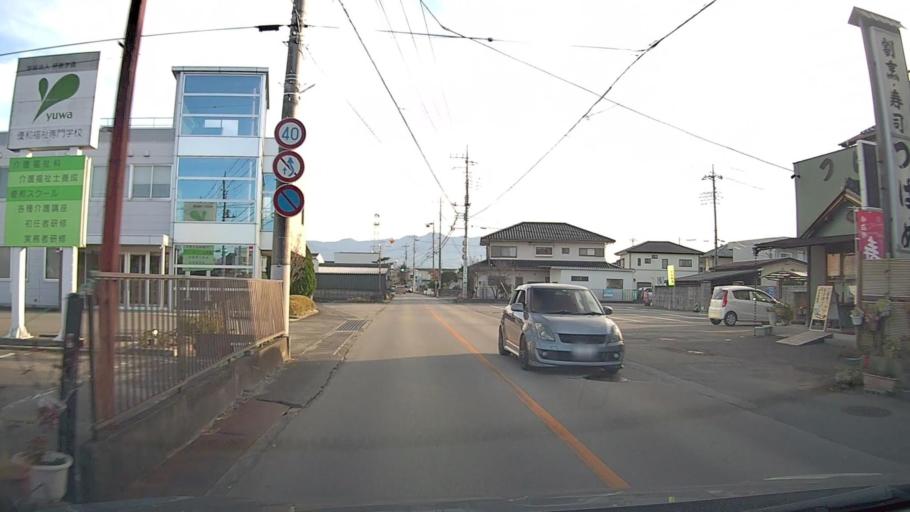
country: JP
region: Yamanashi
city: Ryuo
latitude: 35.6300
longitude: 138.5233
